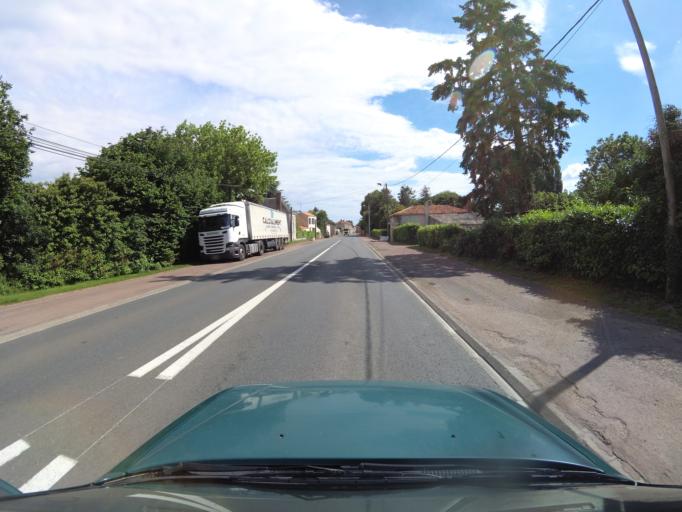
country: FR
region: Pays de la Loire
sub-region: Departement de la Vendee
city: Sainte-Hermine
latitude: 46.5972
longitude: -1.0384
